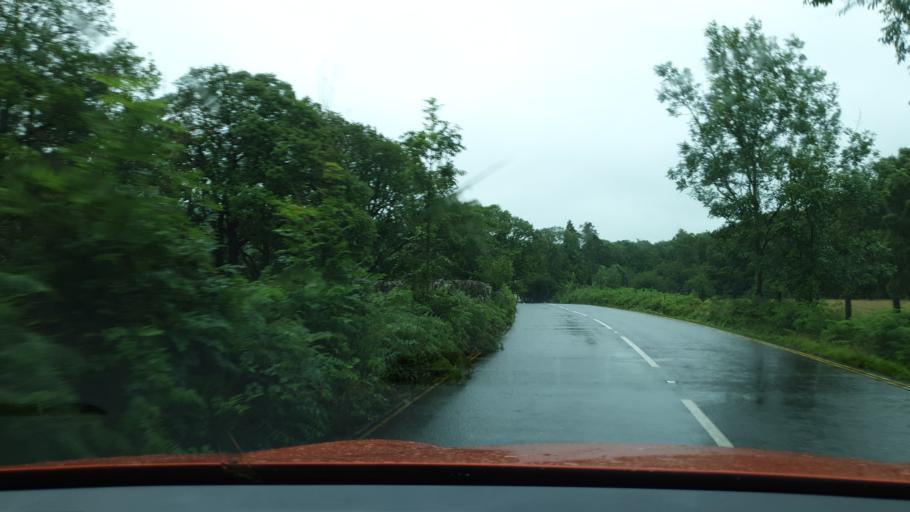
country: GB
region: England
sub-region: Cumbria
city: Ulverston
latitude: 54.3138
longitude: -3.0919
